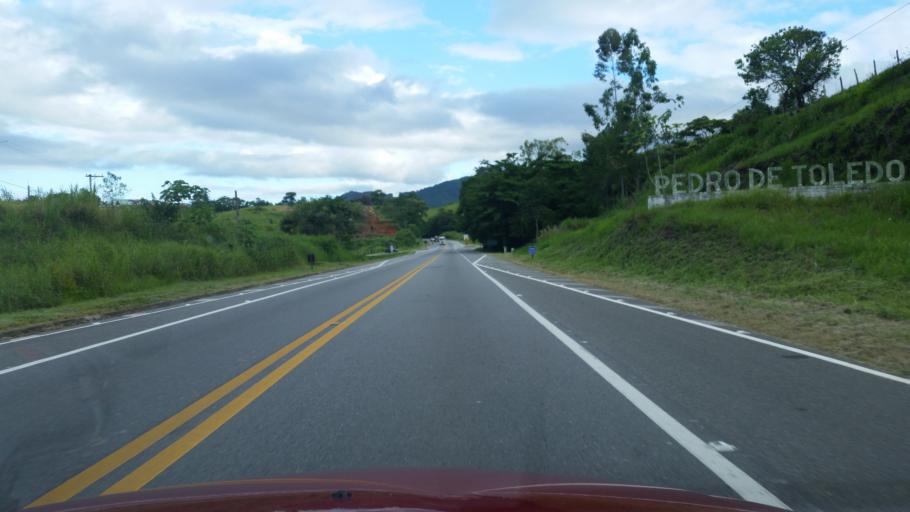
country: BR
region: Sao Paulo
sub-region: Miracatu
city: Miracatu
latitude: -24.2788
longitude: -47.2421
